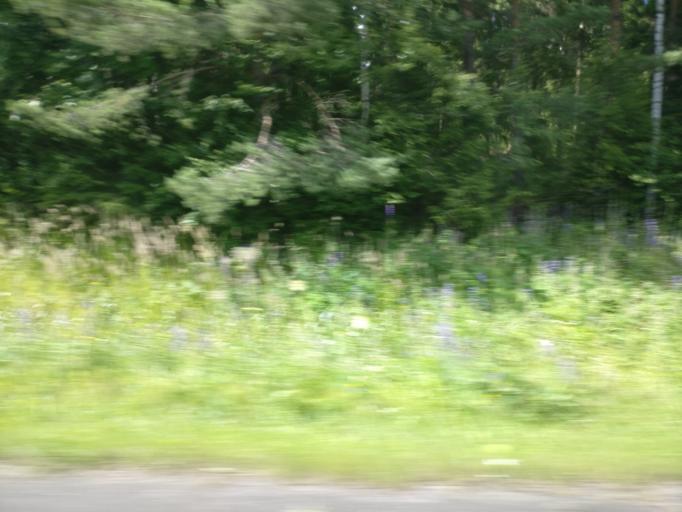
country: FI
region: Uusimaa
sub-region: Helsinki
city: Maentsaelae
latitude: 60.6280
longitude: 25.2515
